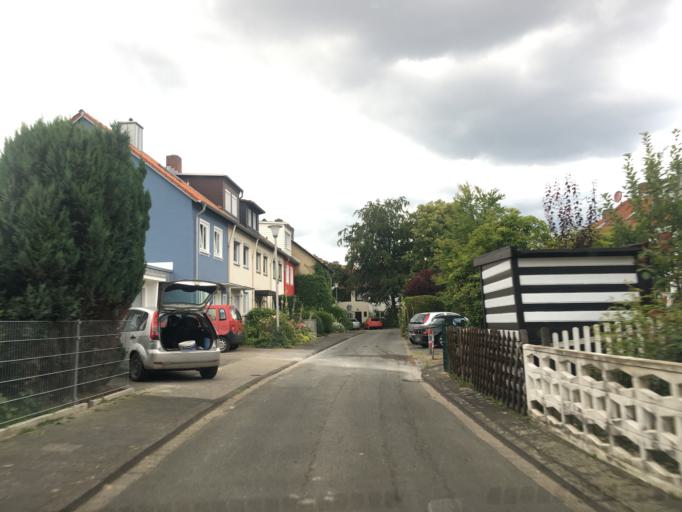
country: DE
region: North Rhine-Westphalia
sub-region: Regierungsbezirk Munster
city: Muenster
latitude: 51.9531
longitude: 7.6694
